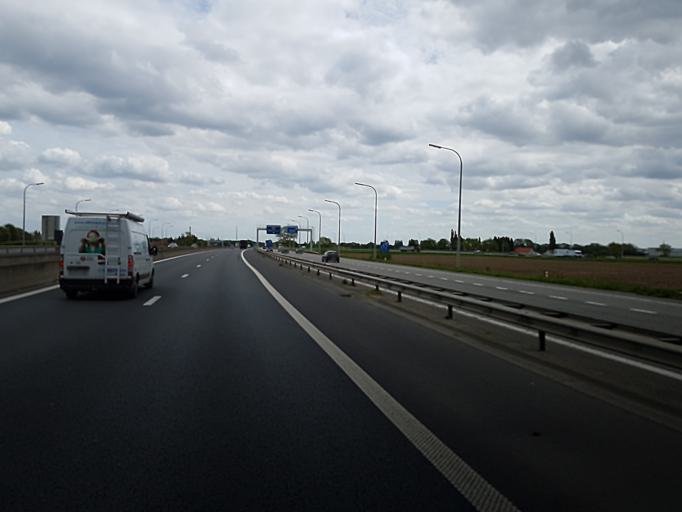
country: BE
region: Flanders
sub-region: Provincie West-Vlaanderen
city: Wevelgem
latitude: 50.8293
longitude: 3.1970
